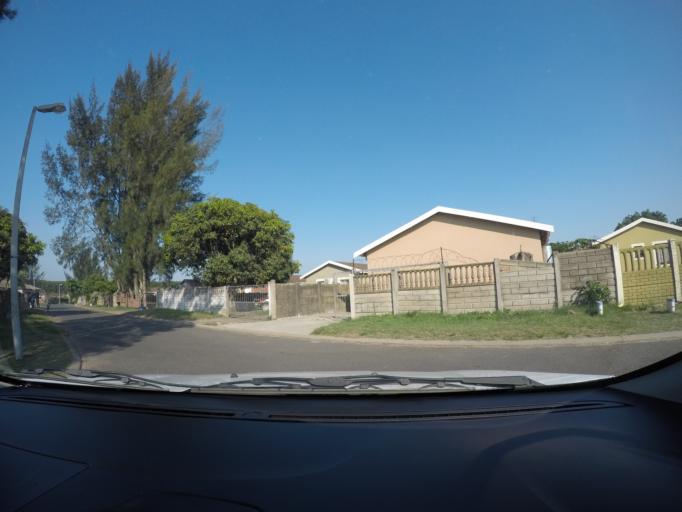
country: ZA
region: KwaZulu-Natal
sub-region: uThungulu District Municipality
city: Richards Bay
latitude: -28.7156
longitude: 32.0384
